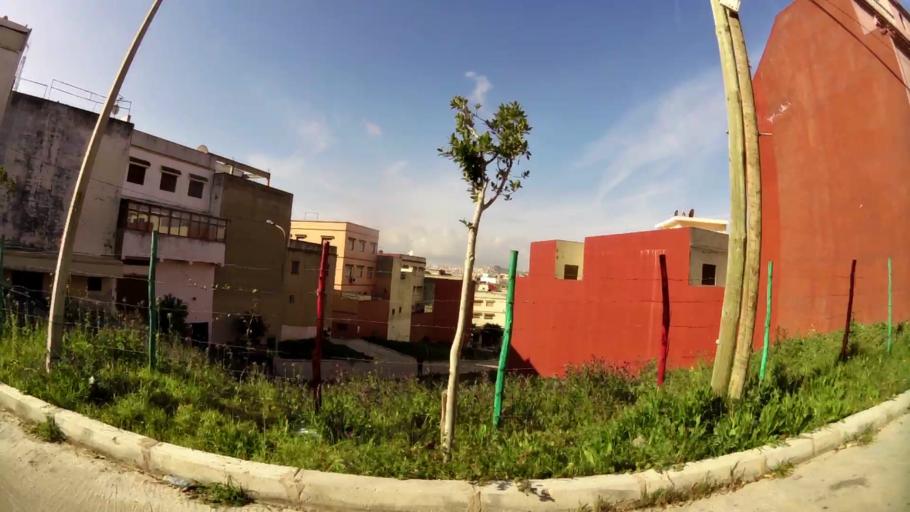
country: MA
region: Tanger-Tetouan
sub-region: Tanger-Assilah
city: Tangier
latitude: 35.7640
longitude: -5.7928
